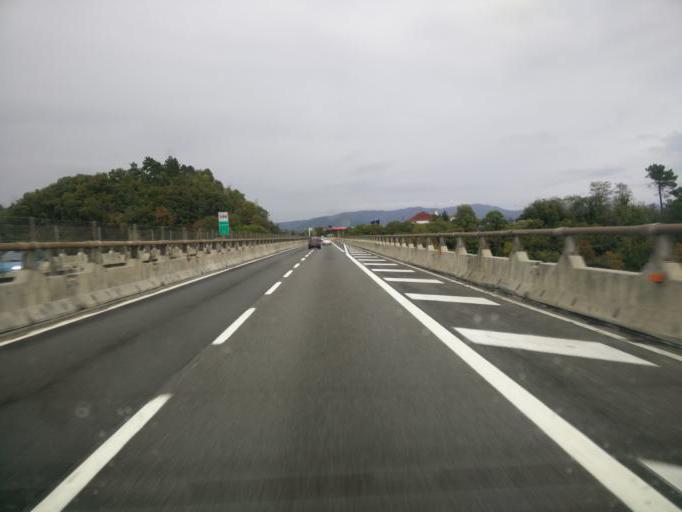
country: IT
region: Tuscany
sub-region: Province of Florence
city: Barberino di Mugello
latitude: 44.0272
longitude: 11.2235
